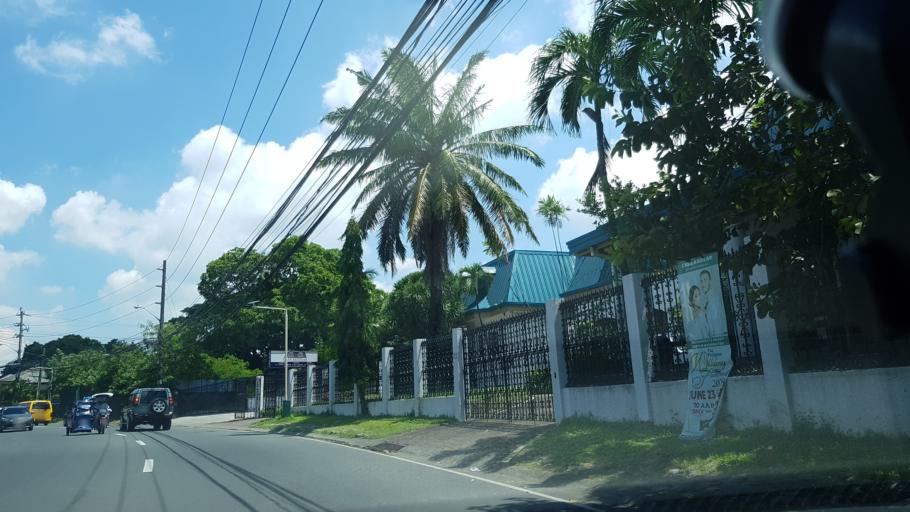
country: PH
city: Sambayanihan People's Village
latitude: 14.4508
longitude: 121.0000
